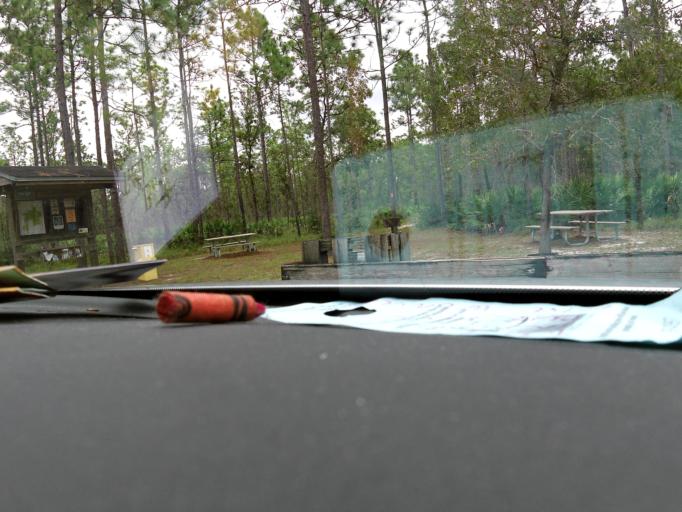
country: US
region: Florida
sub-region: Clay County
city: Middleburg
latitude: 30.1288
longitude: -81.9642
